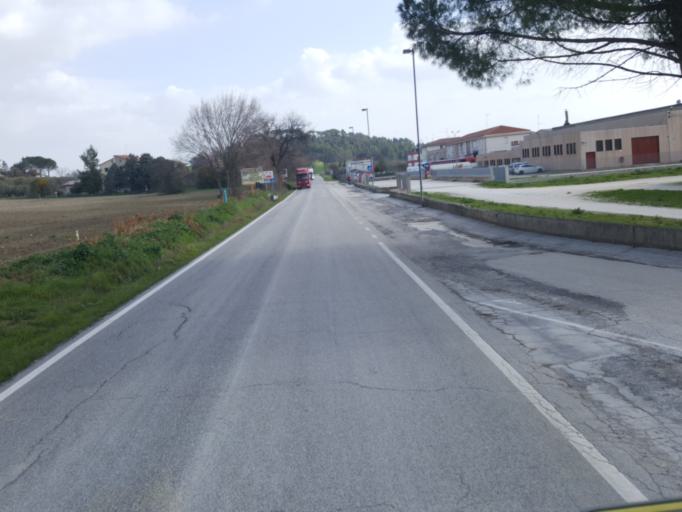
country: IT
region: The Marches
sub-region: Provincia di Macerata
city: Passo di Treia
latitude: 43.2926
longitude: 13.3411
